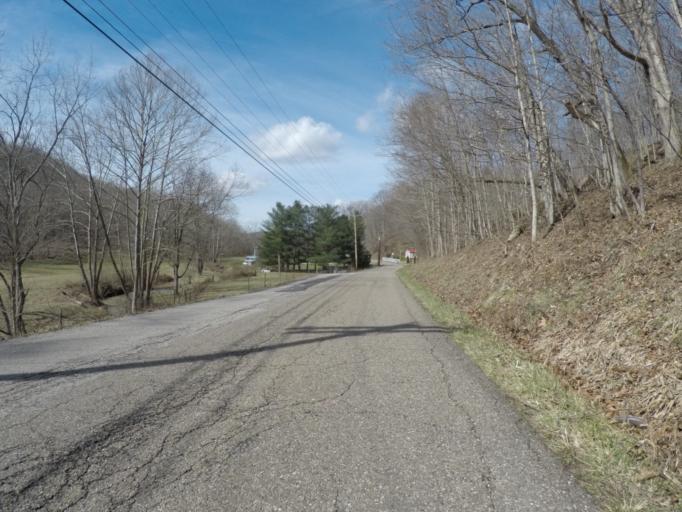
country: US
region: Ohio
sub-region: Lawrence County
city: Burlington
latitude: 38.4781
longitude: -82.5049
